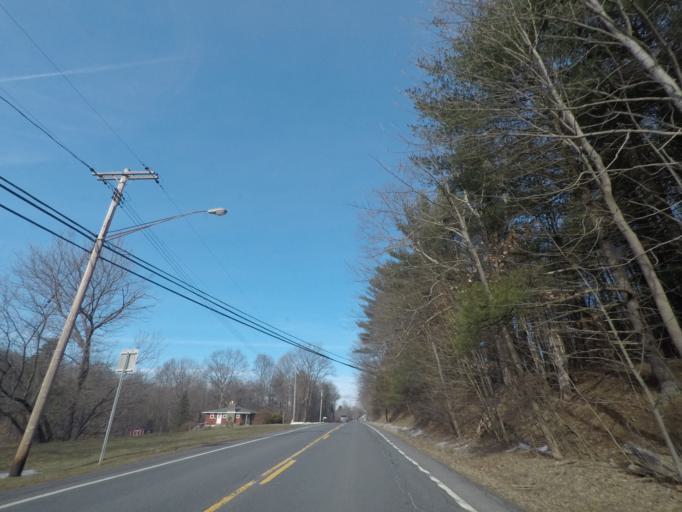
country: US
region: New York
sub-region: Rensselaer County
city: Nassau
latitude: 42.5071
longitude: -73.6137
